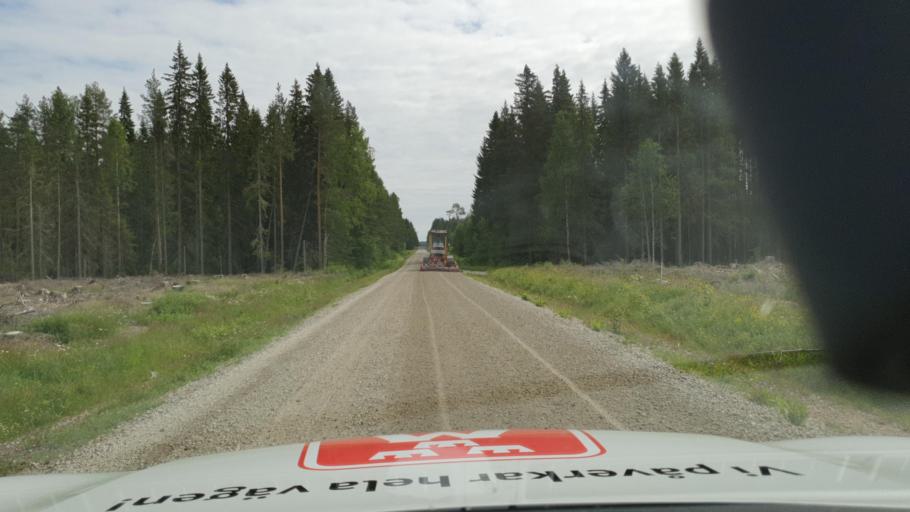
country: SE
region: Vaesterbotten
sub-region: Skelleftea Kommun
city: Forsbacka
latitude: 64.6561
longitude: 20.4101
